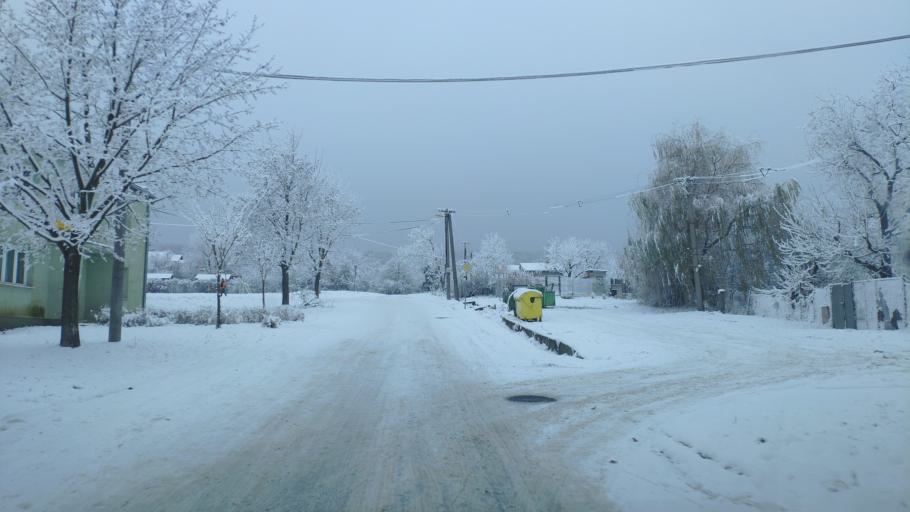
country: SK
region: Kosicky
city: Kosice
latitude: 48.6425
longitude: 21.1976
